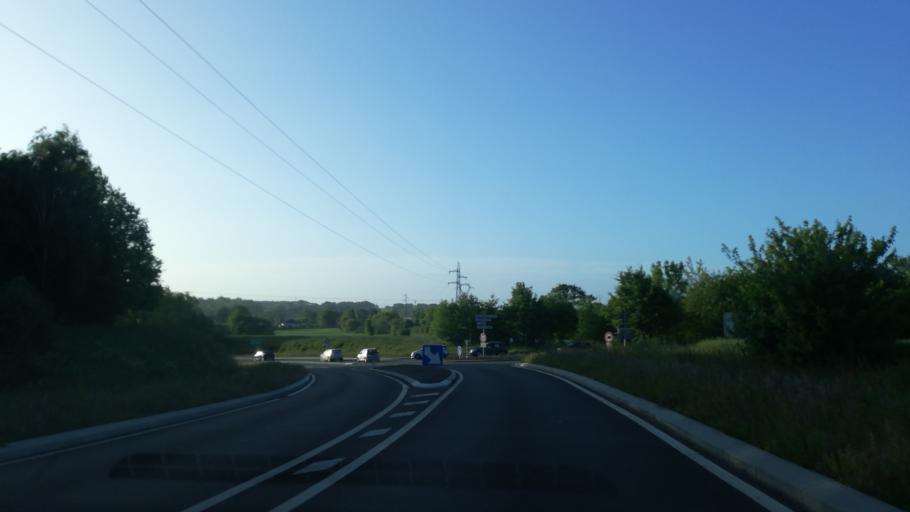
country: FR
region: Brittany
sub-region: Departement d'Ille-et-Vilaine
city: Saint-Gilles
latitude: 48.1506
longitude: -1.7997
